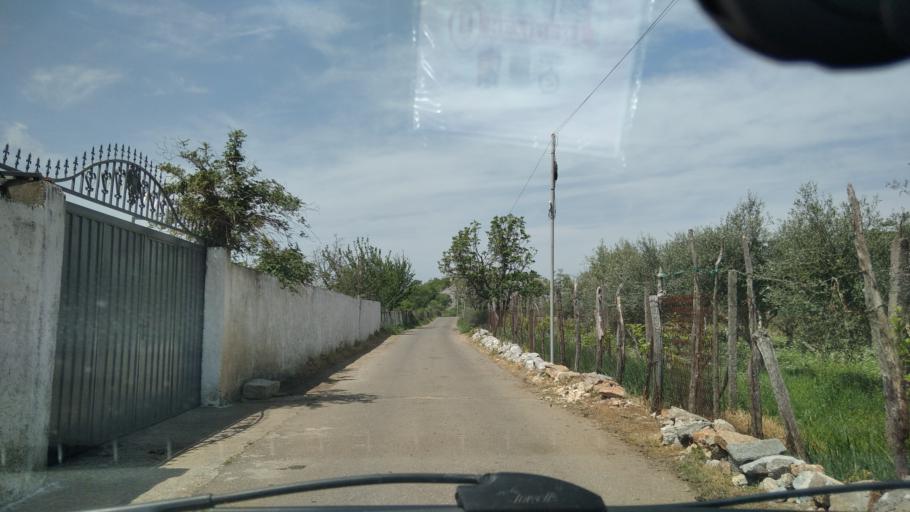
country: AL
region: Shkoder
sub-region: Rrethi i Malesia e Madhe
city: Gruemire
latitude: 42.1495
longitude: 19.5370
